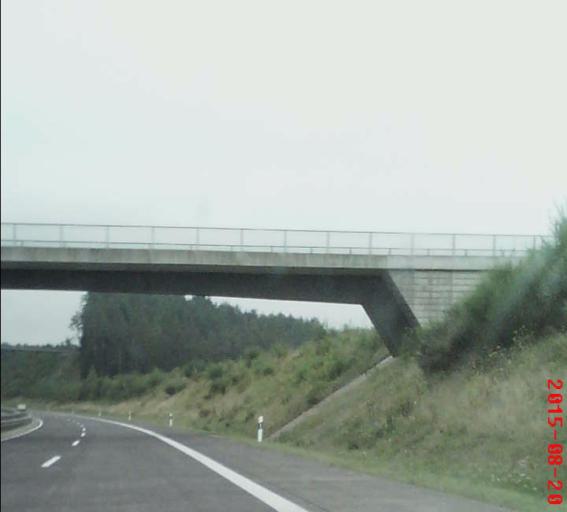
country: DE
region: Thuringia
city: Schleusingen
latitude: 50.4978
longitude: 10.7942
